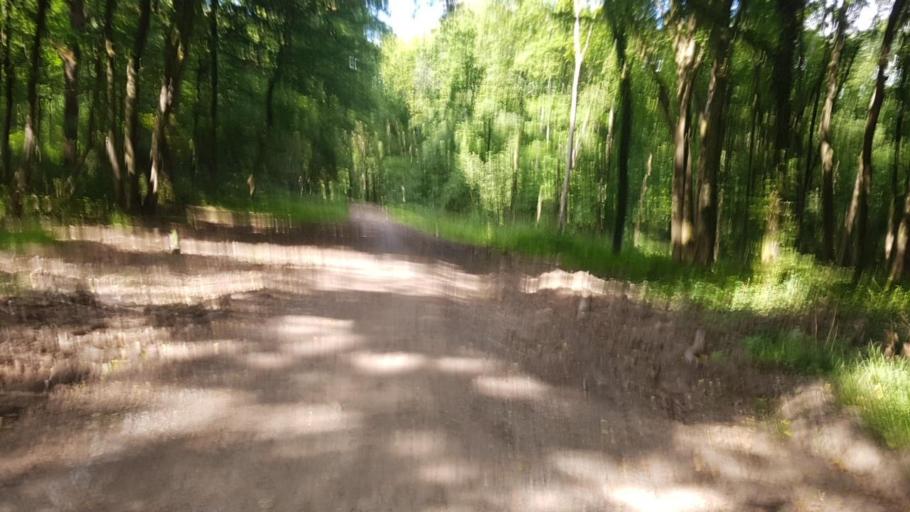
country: BE
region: Wallonia
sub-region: Province du Hainaut
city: Charleroi
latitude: 50.3678
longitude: 4.4551
